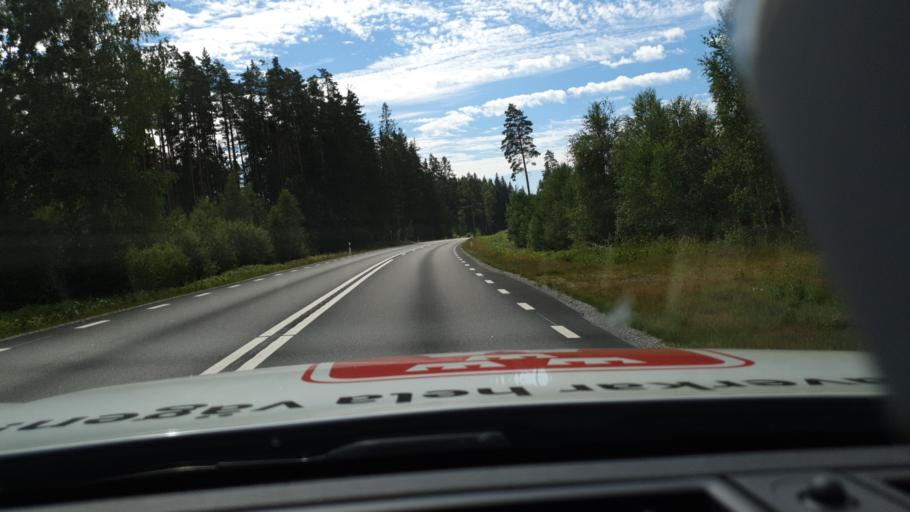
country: SE
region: Joenkoeping
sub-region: Savsjo Kommun
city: Stockaryd
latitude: 57.2886
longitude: 14.5234
